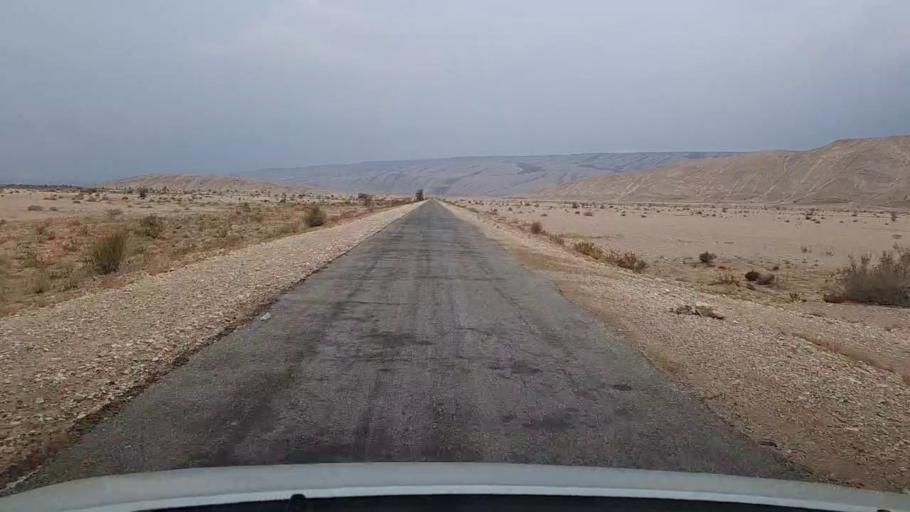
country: PK
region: Sindh
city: Sehwan
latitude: 26.2428
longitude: 67.7144
